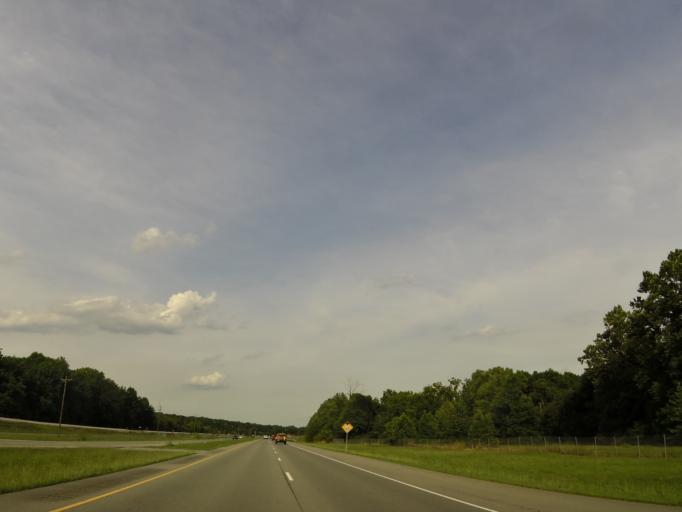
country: US
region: Tennessee
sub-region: Humphreys County
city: Waverly
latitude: 36.0861
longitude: -87.8138
